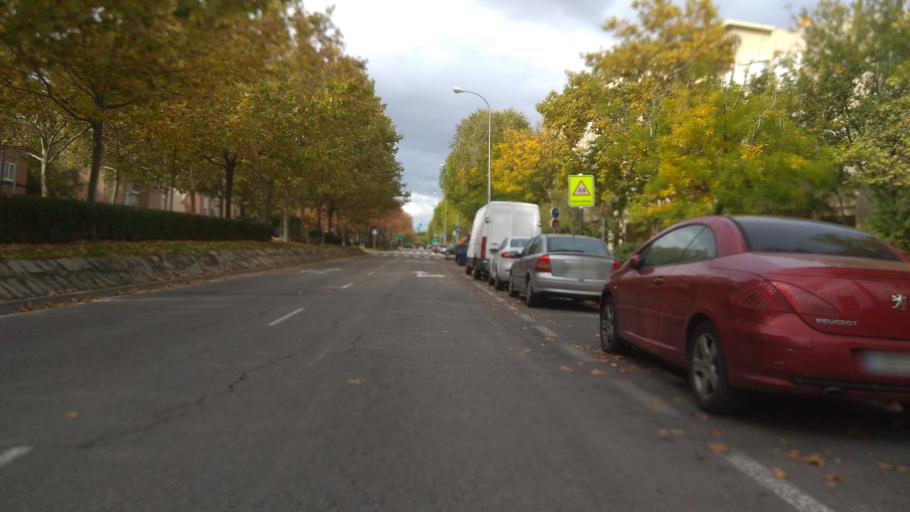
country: ES
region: Madrid
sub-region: Provincia de Madrid
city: Vicalvaro
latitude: 40.4077
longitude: -3.6046
